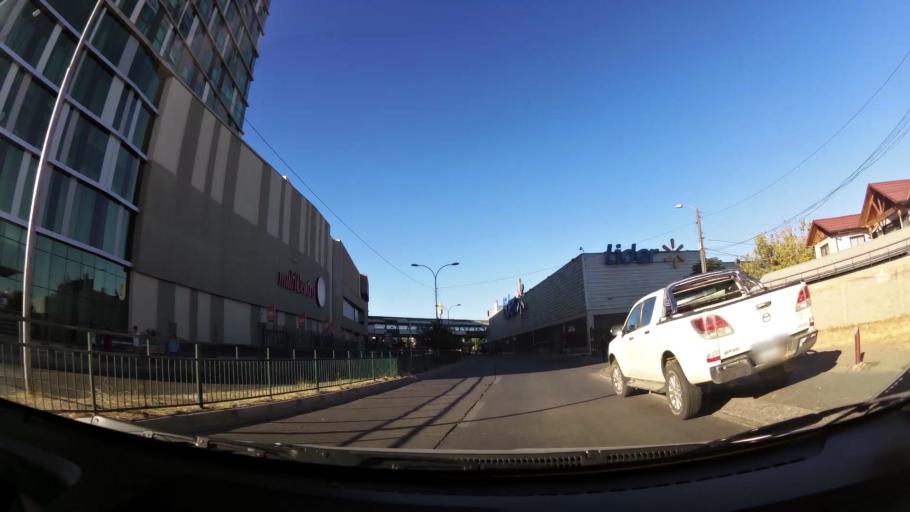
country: CL
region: O'Higgins
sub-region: Provincia de Cachapoal
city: Rancagua
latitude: -34.1718
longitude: -70.7156
